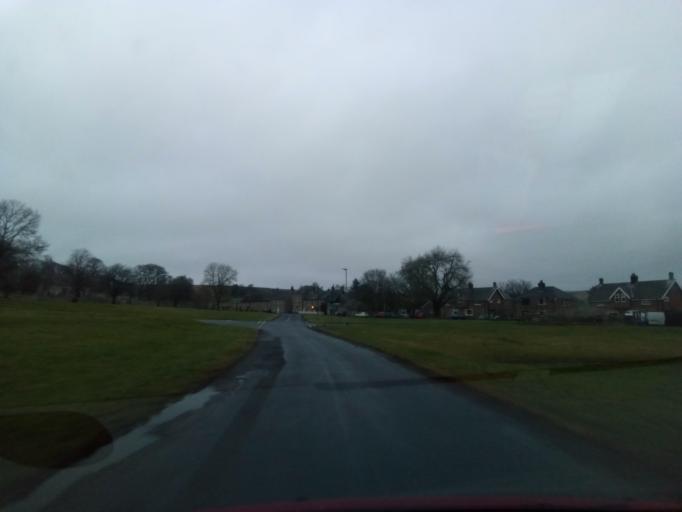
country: GB
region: England
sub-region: Northumberland
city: Otterburn
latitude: 55.2318
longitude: -2.1023
